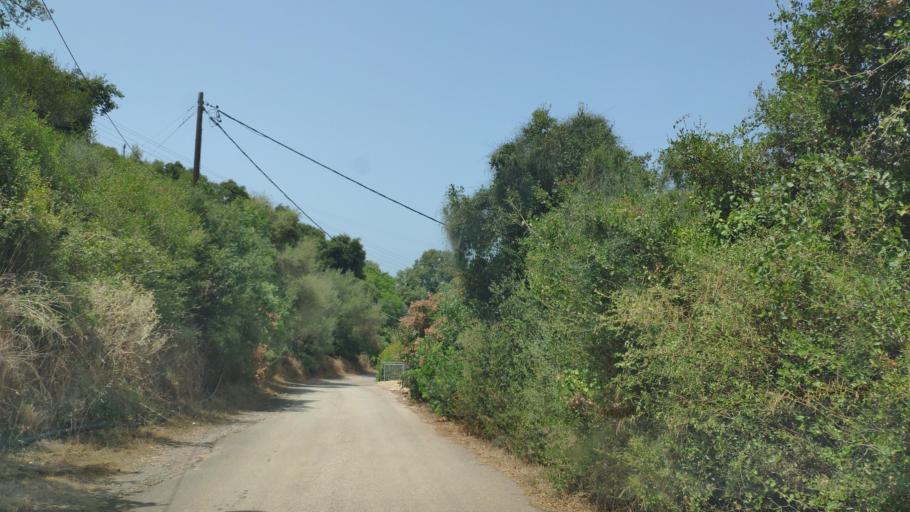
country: GR
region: West Greece
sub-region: Nomos Aitolias kai Akarnanias
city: Amfilochia
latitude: 38.8686
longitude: 21.0734
